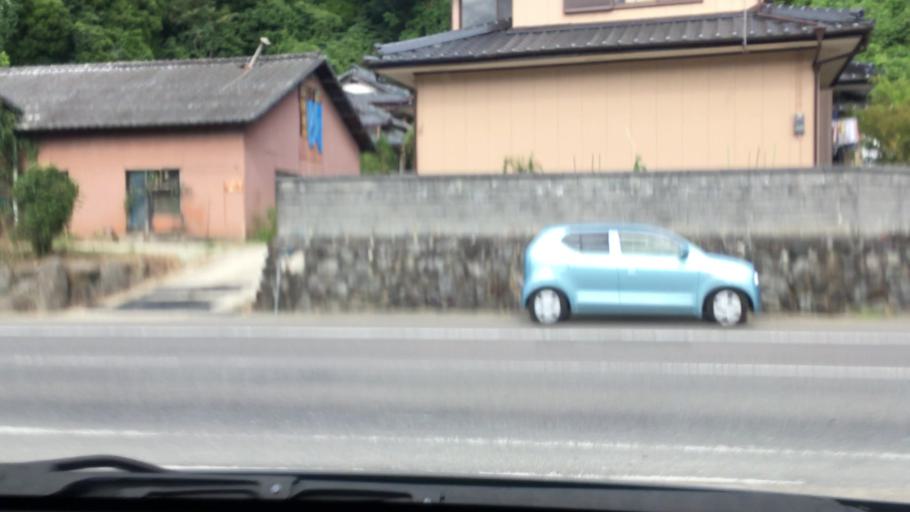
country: JP
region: Saga Prefecture
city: Takeocho-takeo
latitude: 33.1774
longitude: 130.0375
